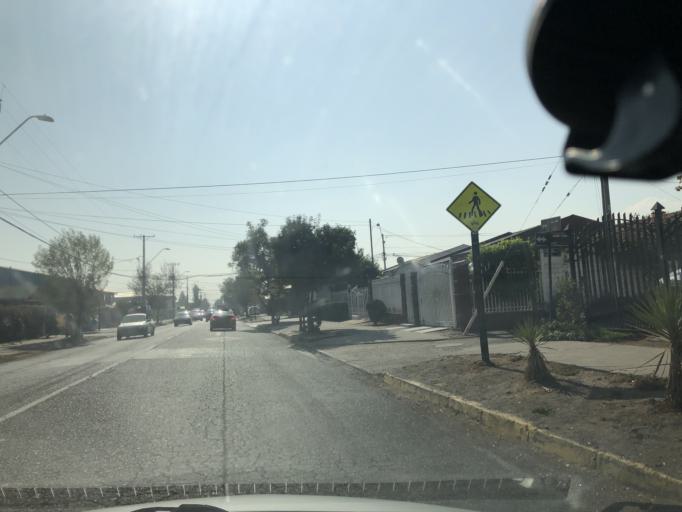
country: CL
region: Santiago Metropolitan
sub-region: Provincia de Cordillera
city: Puente Alto
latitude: -33.6003
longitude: -70.5719
